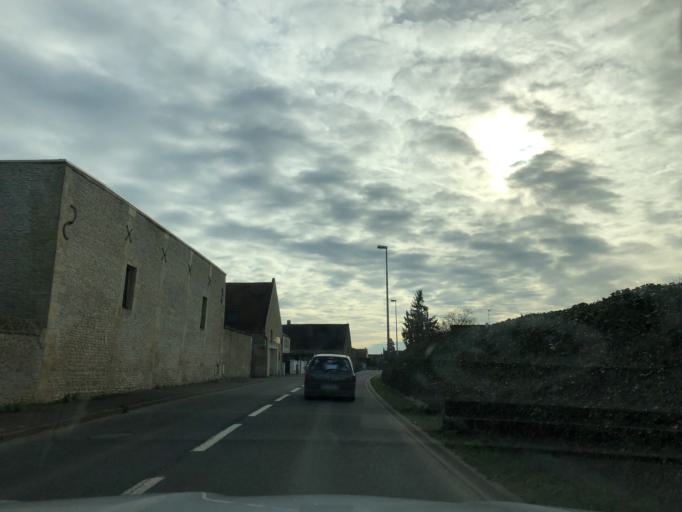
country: FR
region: Lower Normandy
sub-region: Departement du Calvados
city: Beuville
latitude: 49.2477
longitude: -0.3303
